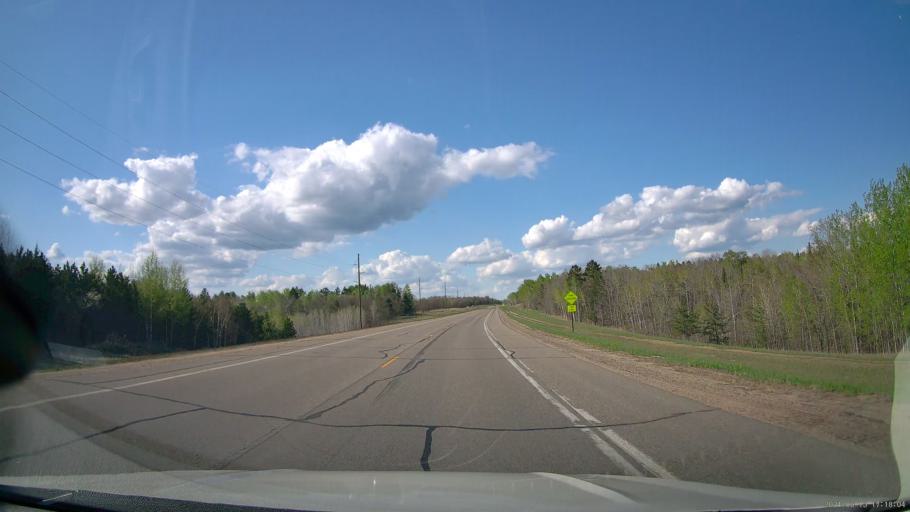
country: US
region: Minnesota
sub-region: Hubbard County
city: Park Rapids
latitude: 46.9553
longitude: -95.0184
